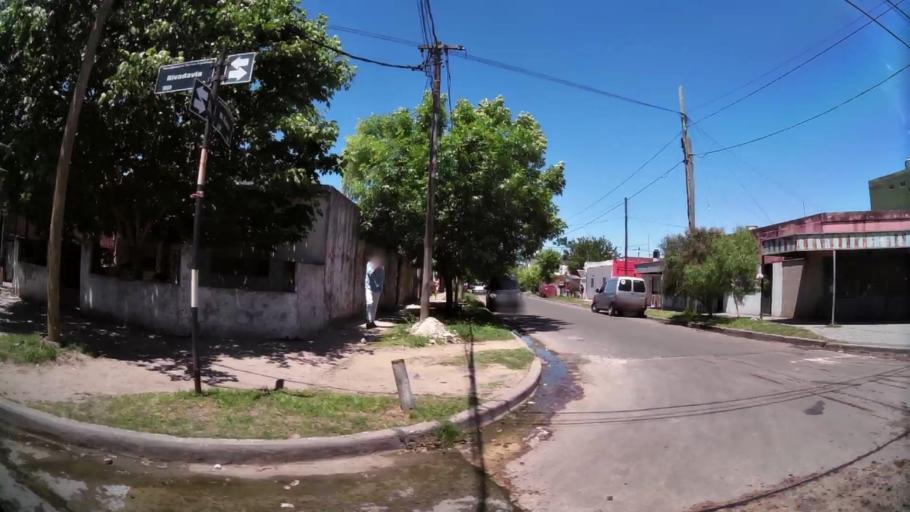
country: AR
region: Buenos Aires
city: Hurlingham
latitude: -34.5095
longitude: -58.7032
